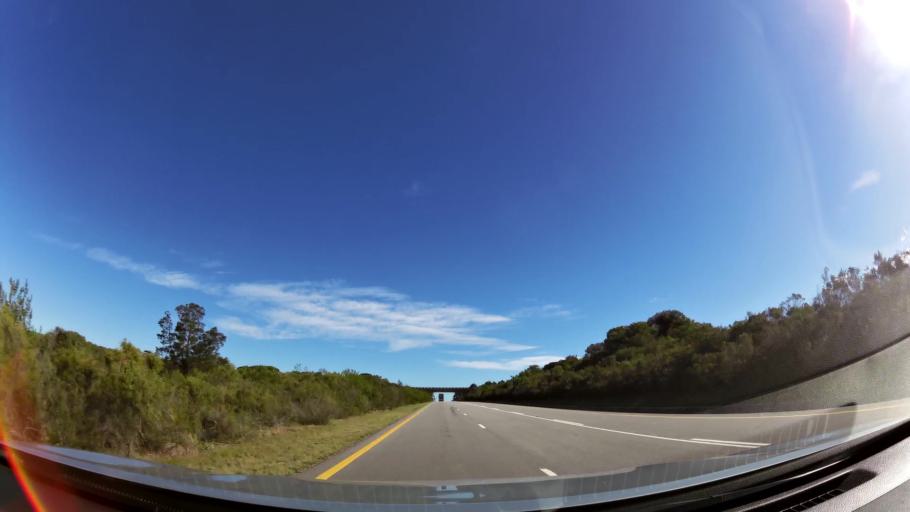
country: ZA
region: Eastern Cape
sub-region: Cacadu District Municipality
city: Kruisfontein
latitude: -34.0178
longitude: 24.6232
